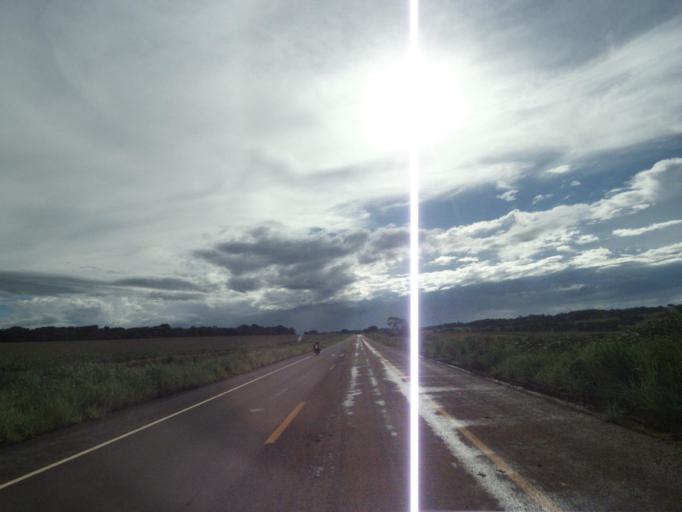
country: BR
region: Goias
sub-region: Jaragua
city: Jaragua
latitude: -15.9029
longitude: -49.5408
